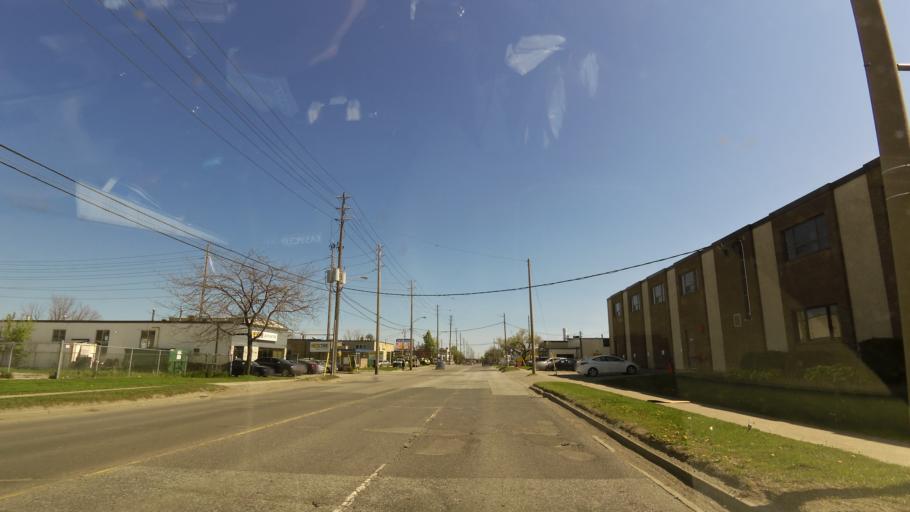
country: CA
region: Ontario
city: Etobicoke
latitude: 43.6284
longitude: -79.5433
